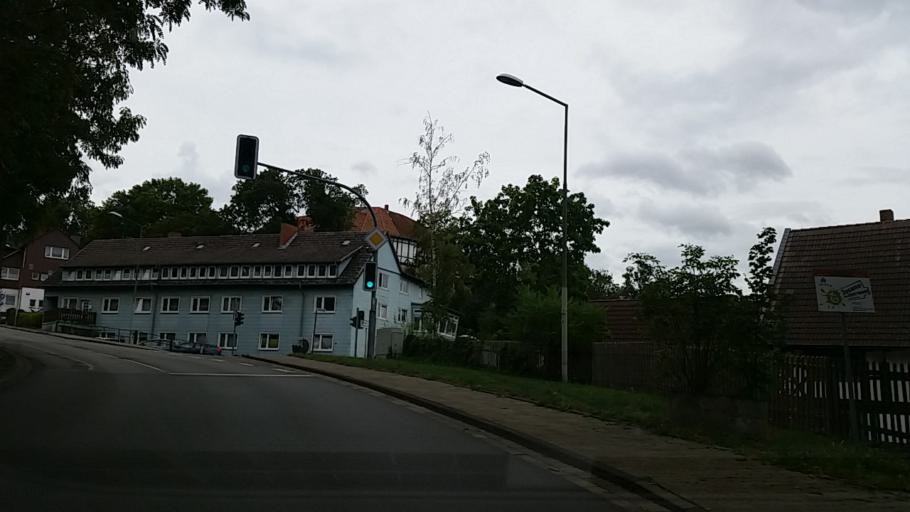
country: DE
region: Lower Saxony
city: Vienenburg
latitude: 51.9492
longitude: 10.5638
